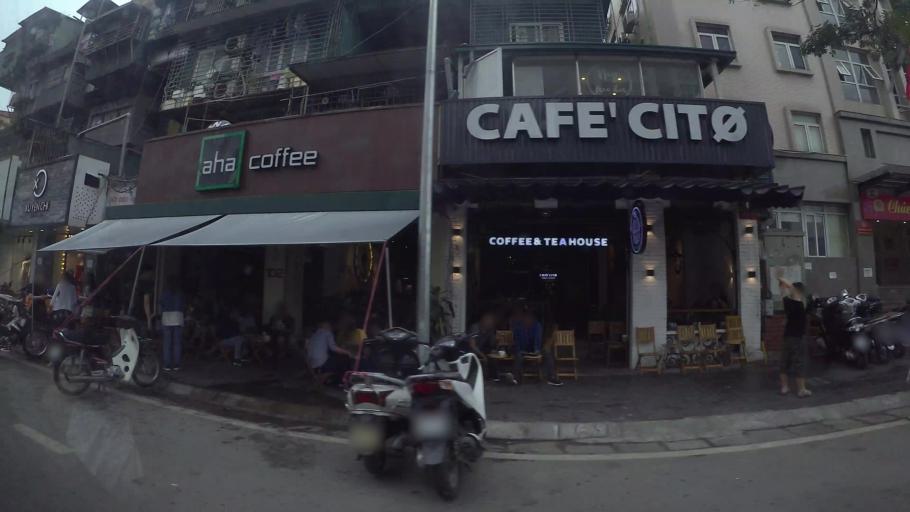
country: VN
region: Ha Noi
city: Dong Da
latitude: 21.0104
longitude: 105.8361
